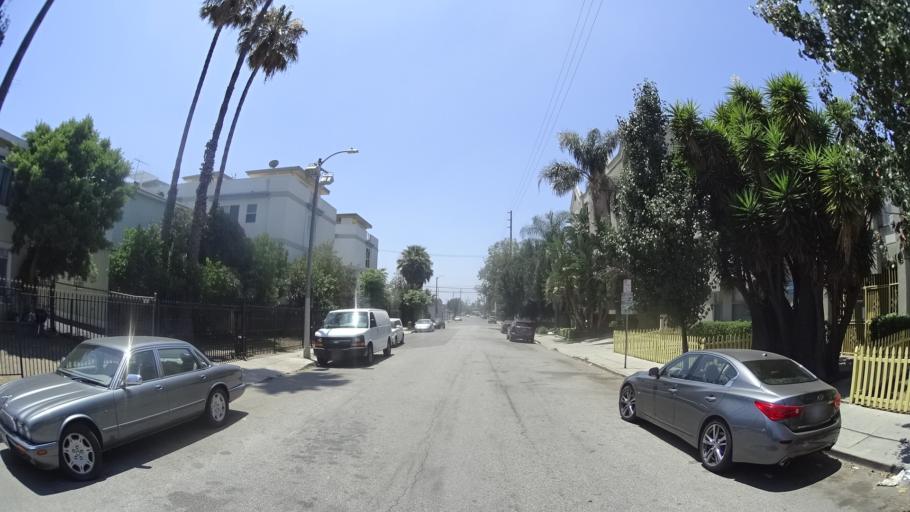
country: US
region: California
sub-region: Los Angeles County
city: Hollywood
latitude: 34.0933
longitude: -118.3375
